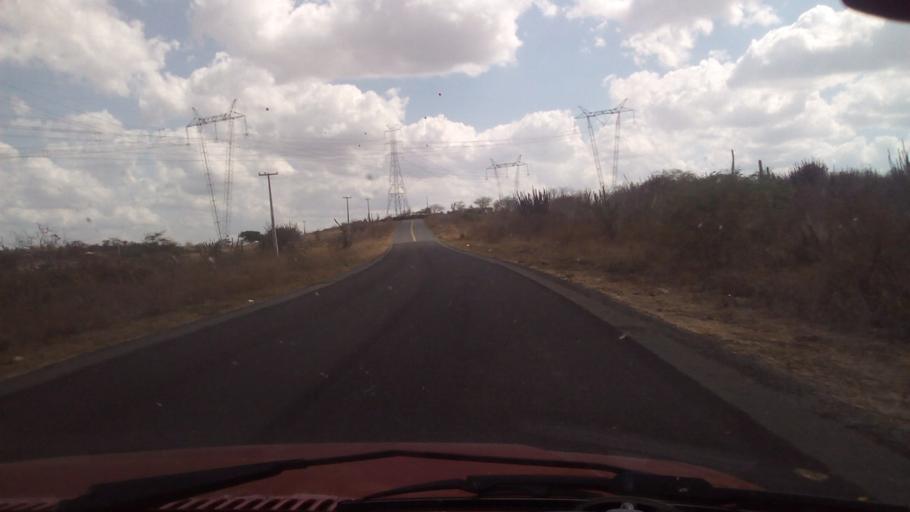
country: BR
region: Paraiba
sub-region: Cacimba De Dentro
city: Cacimba de Dentro
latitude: -6.7049
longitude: -35.7272
